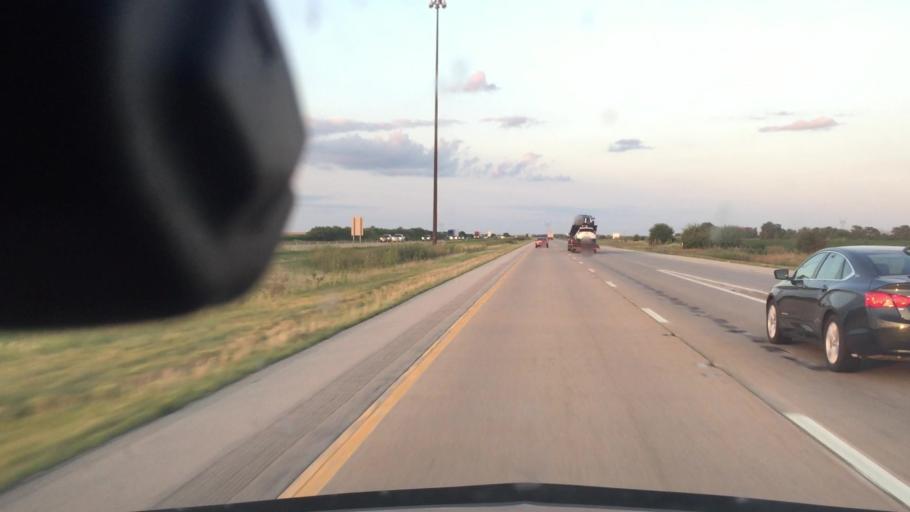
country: US
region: Illinois
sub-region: Livingston County
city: Dwight
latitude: 41.1179
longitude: -88.4093
